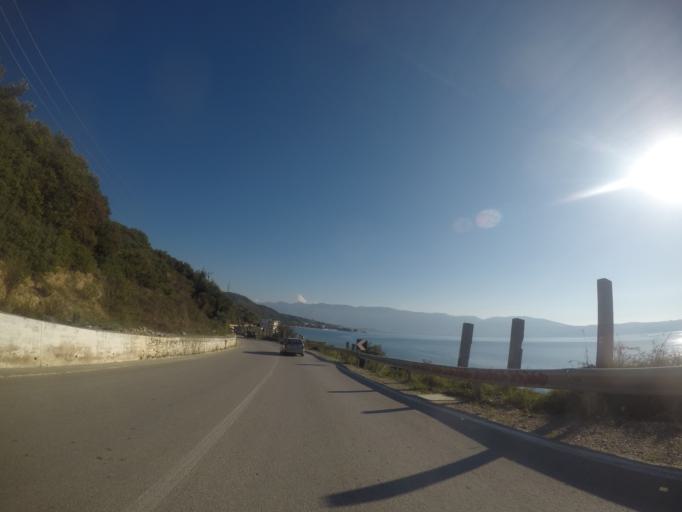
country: AL
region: Vlore
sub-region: Rrethi i Vlores
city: Orikum
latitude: 40.3955
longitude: 19.4783
